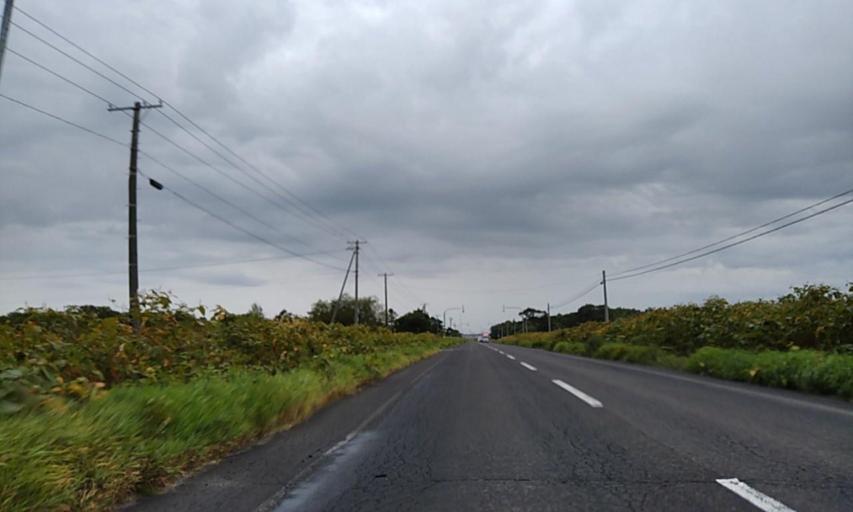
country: JP
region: Hokkaido
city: Nayoro
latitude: 44.6502
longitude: 142.8878
